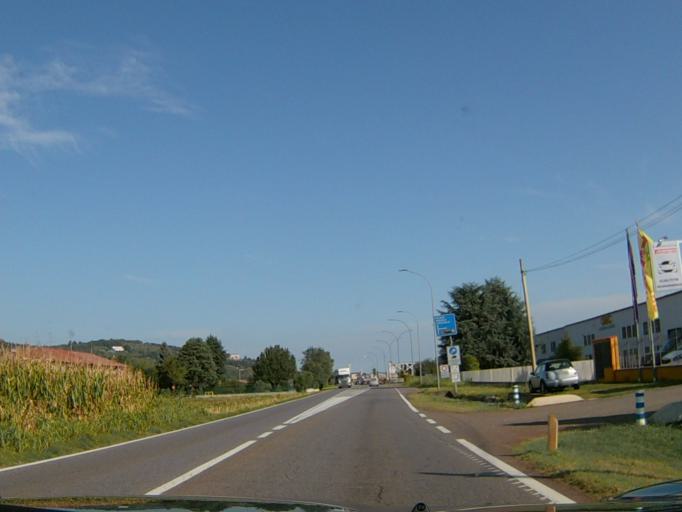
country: IT
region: Lombardy
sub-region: Provincia di Brescia
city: Cologne
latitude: 45.5714
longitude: 9.9564
